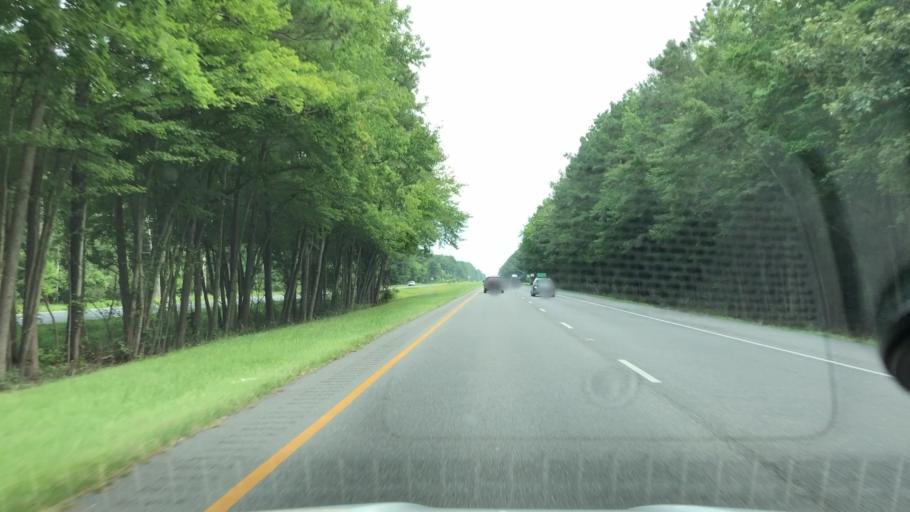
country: US
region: Maryland
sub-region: Worcester County
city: Pocomoke City
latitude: 38.1069
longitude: -75.6399
